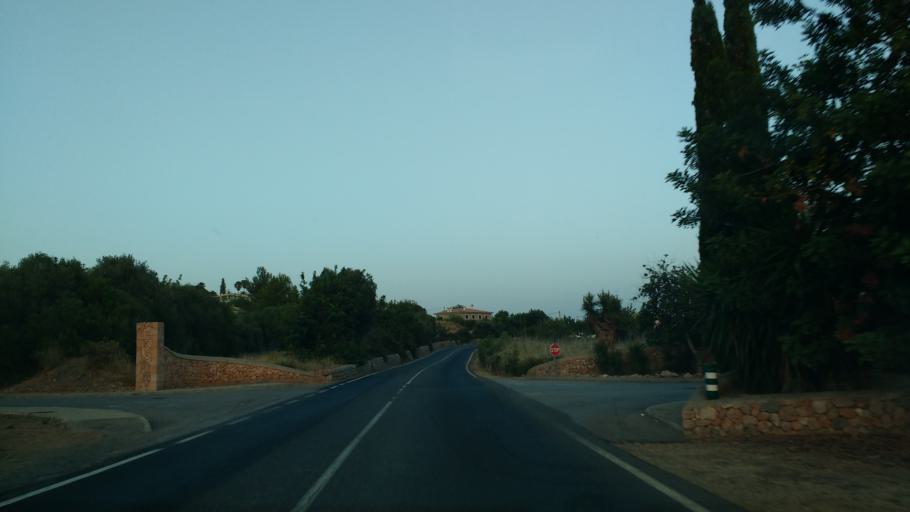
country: ES
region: Balearic Islands
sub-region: Illes Balears
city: Bunyola
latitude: 39.6674
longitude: 2.6854
